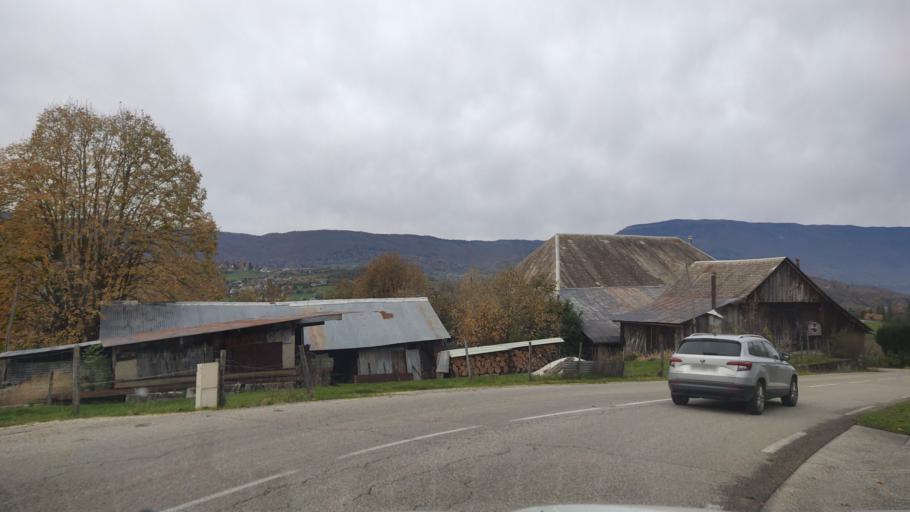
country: FR
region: Rhone-Alpes
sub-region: Departement de la Savoie
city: Jacob-Bellecombette
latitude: 45.5442
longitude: 5.9040
